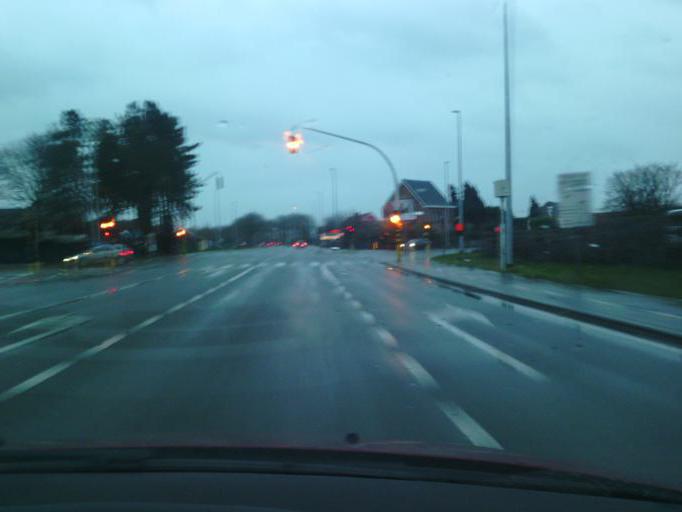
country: BE
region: Flanders
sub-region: Provincie Oost-Vlaanderen
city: Lokeren
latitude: 51.0996
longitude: 3.9728
